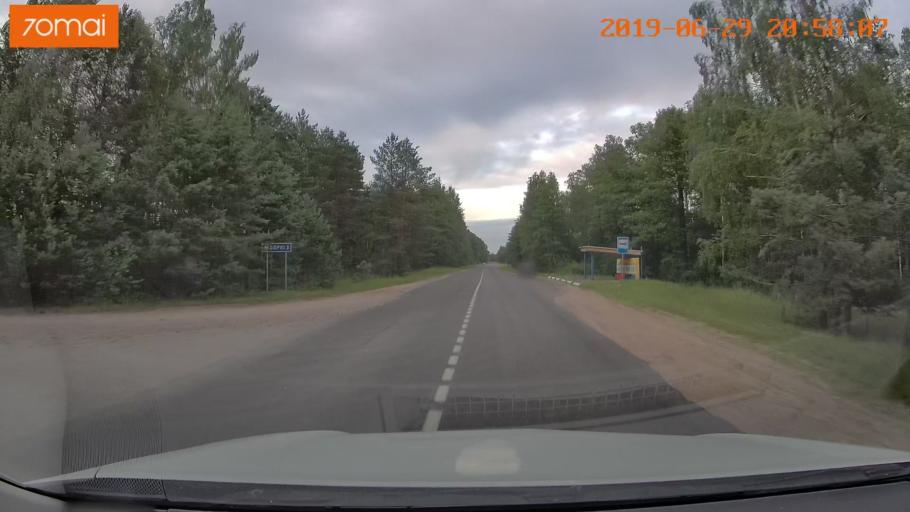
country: BY
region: Brest
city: Hantsavichy
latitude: 52.7271
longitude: 26.3801
